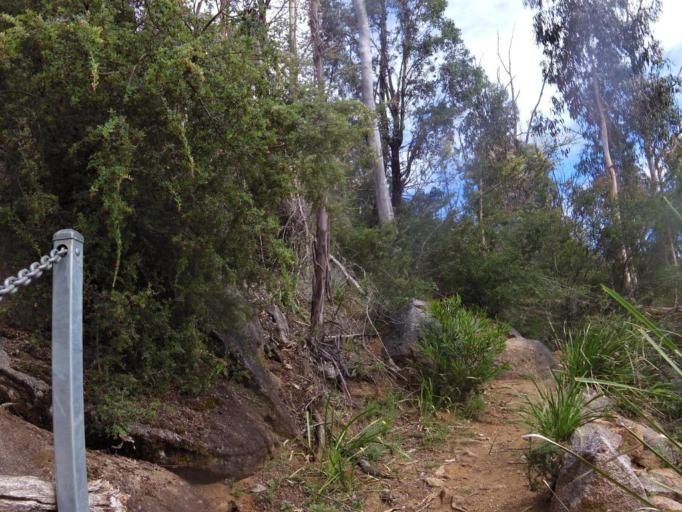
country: AU
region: Victoria
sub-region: Murrindindi
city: Alexandra
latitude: -37.4012
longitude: 145.5734
